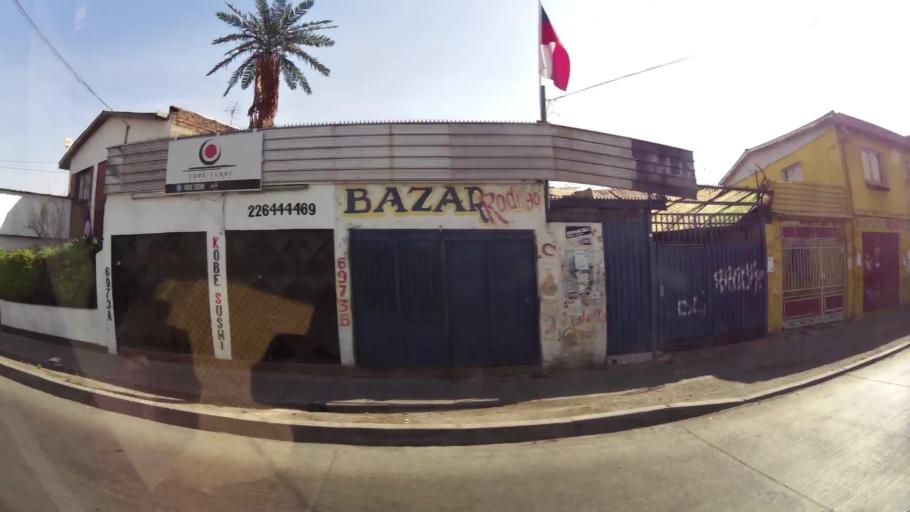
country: CL
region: Santiago Metropolitan
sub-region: Provincia de Santiago
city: Lo Prado
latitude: -33.4291
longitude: -70.7318
